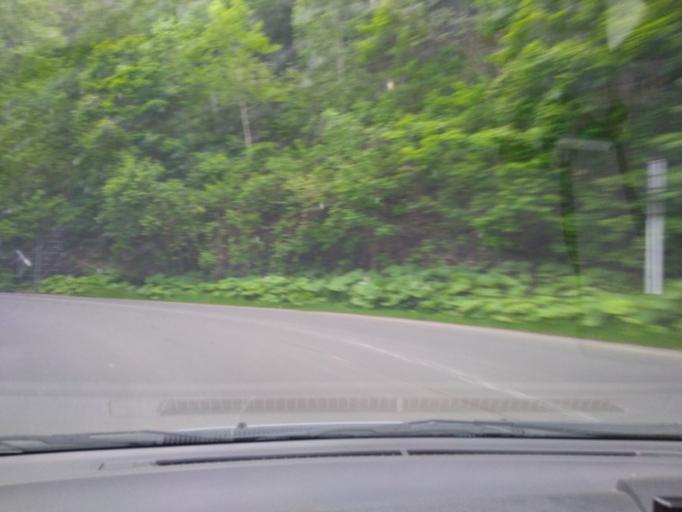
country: JP
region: Hokkaido
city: Shimo-furano
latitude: 43.1409
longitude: 142.4628
